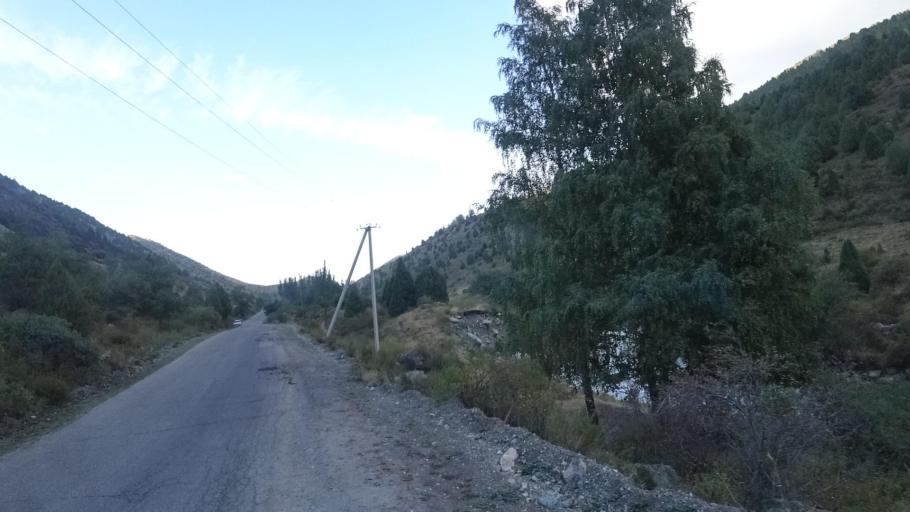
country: KG
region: Chuy
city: Bishkek
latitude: 42.6173
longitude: 74.4857
